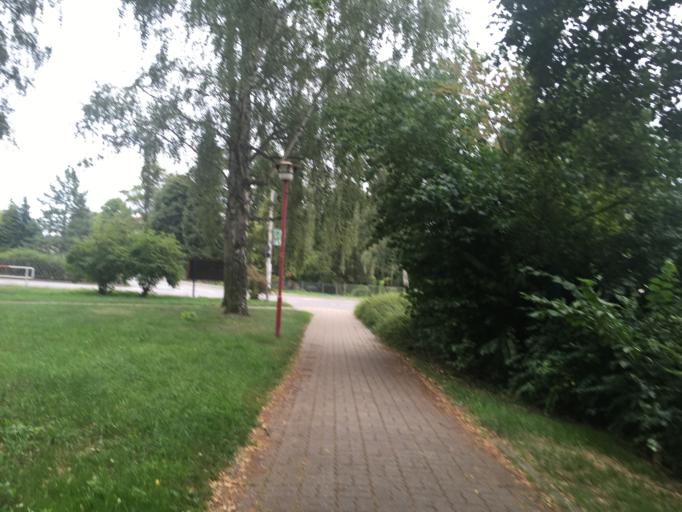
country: DE
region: Saxony
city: Glauchau
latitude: 50.8192
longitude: 12.5566
